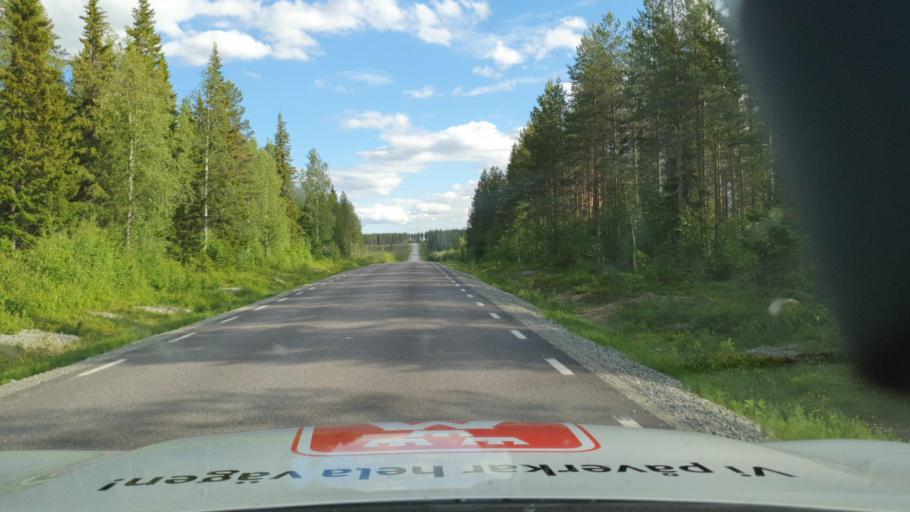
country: SE
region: Vaesterbotten
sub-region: Skelleftea Kommun
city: Langsele
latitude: 64.7103
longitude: 19.9852
